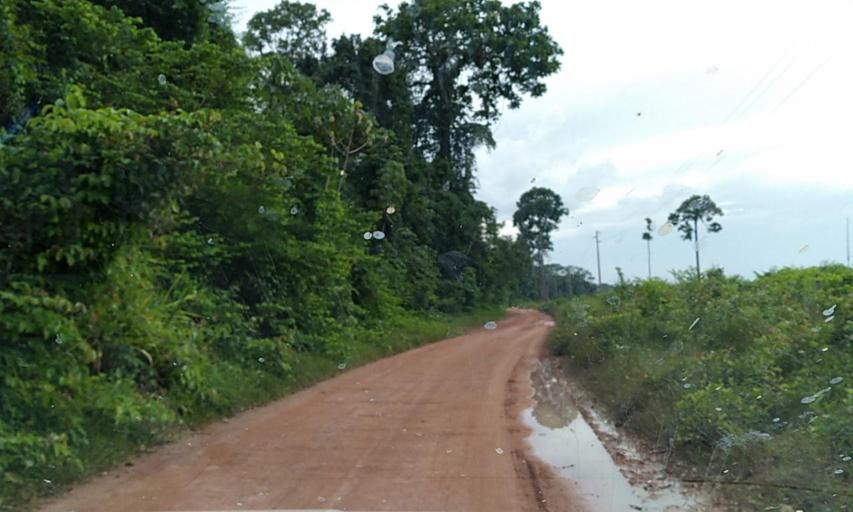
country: BR
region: Para
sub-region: Senador Jose Porfirio
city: Senador Jose Porfirio
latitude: -2.5442
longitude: -51.8602
